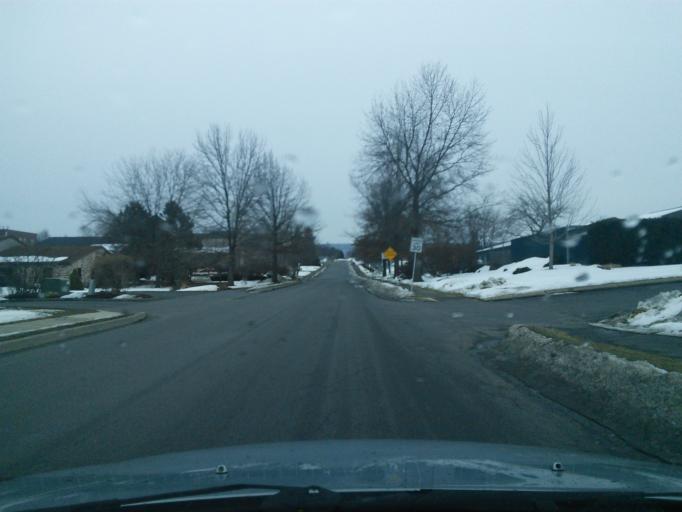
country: US
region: Pennsylvania
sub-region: Centre County
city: Pine Grove Mills
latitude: 40.7663
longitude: -77.8823
